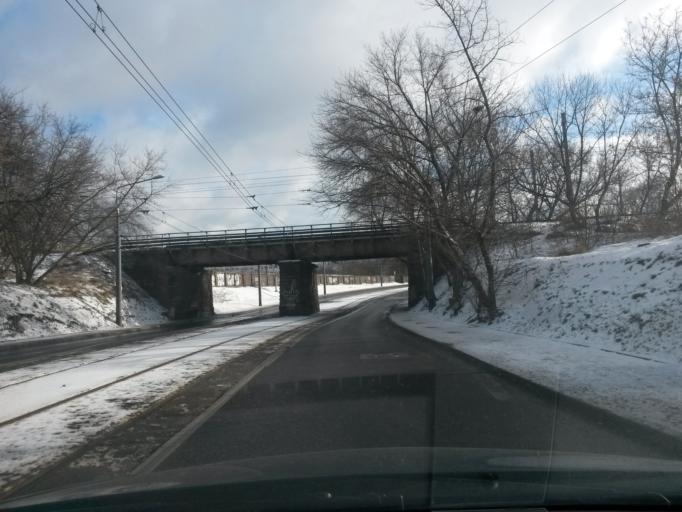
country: PL
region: Masovian Voivodeship
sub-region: Warszawa
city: Wola
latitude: 52.2474
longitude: 20.9585
